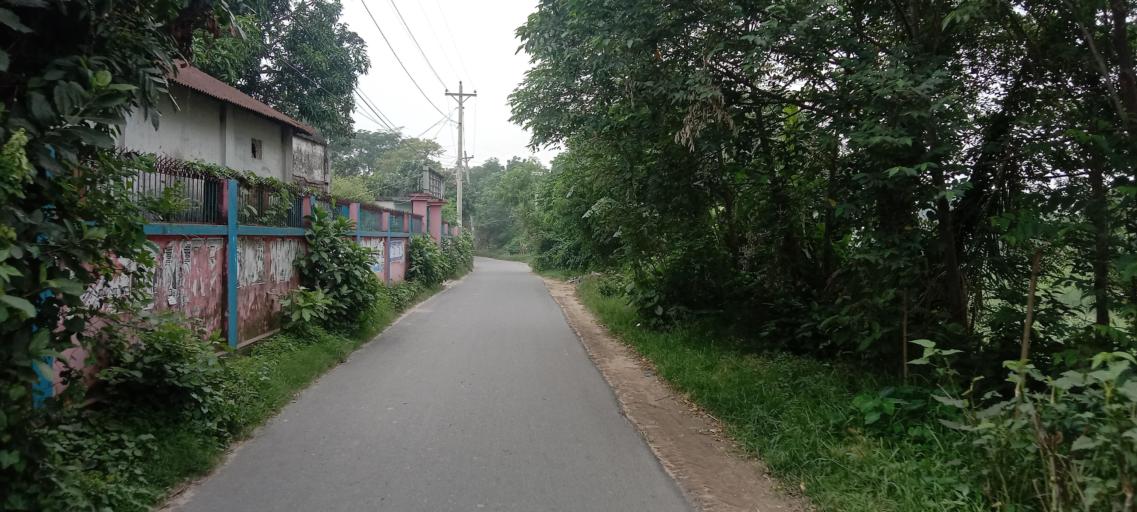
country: BD
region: Dhaka
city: Azimpur
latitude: 23.7445
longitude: 90.3100
